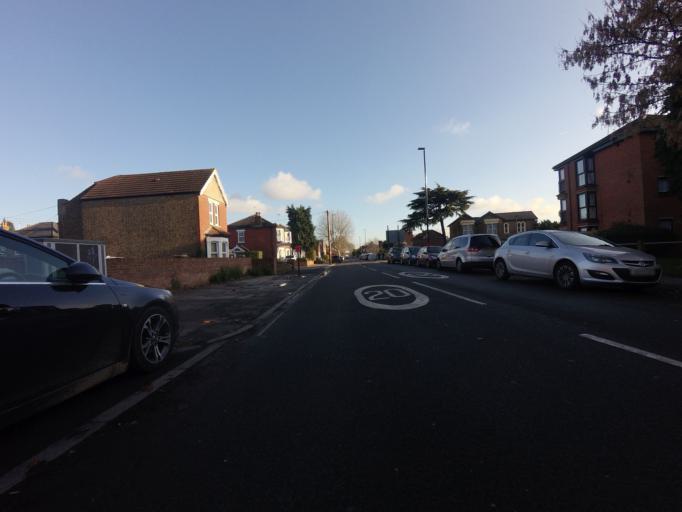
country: GB
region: England
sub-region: Greater London
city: Feltham
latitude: 51.4472
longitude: -0.4054
